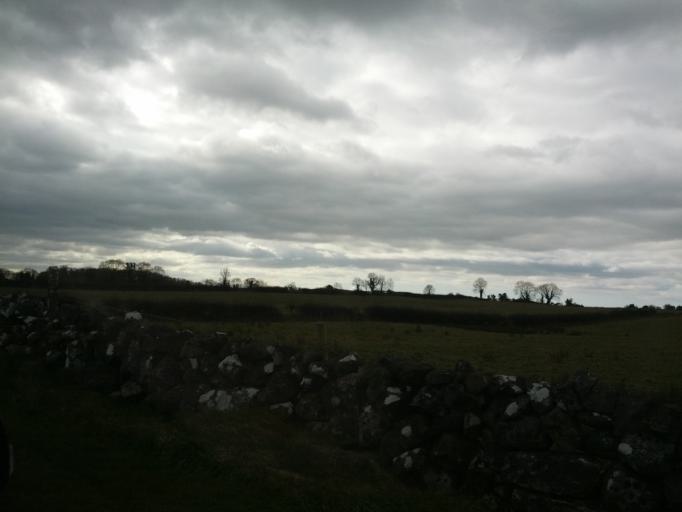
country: IE
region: Connaught
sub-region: County Galway
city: Athenry
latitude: 53.3950
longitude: -8.6415
